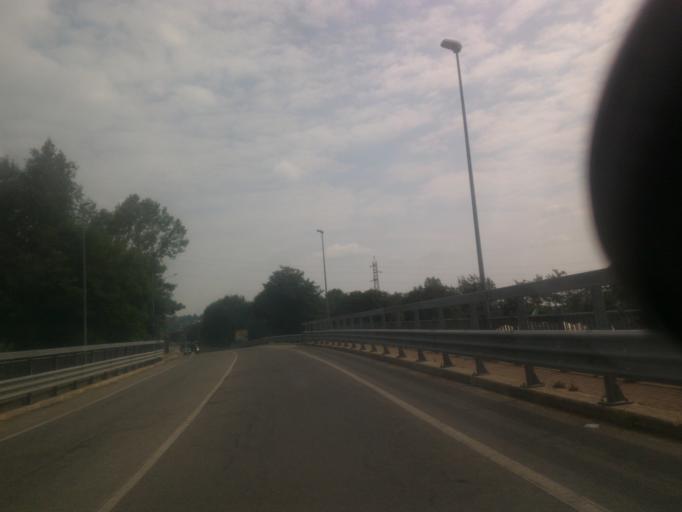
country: IT
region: Piedmont
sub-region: Provincia di Torino
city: San Secondo di Pinerolo
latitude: 44.8749
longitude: 7.3106
